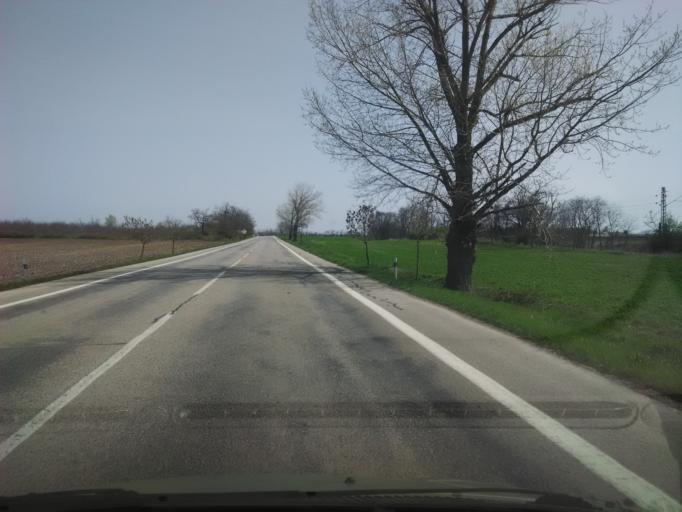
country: SK
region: Nitriansky
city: Sellye
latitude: 48.1465
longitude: 17.9683
